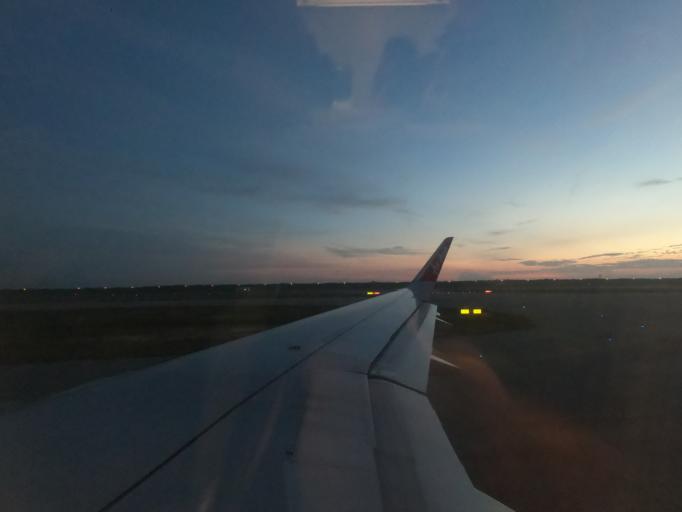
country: MY
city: Sungai Pelek New Village
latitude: 2.7350
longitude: 101.6830
